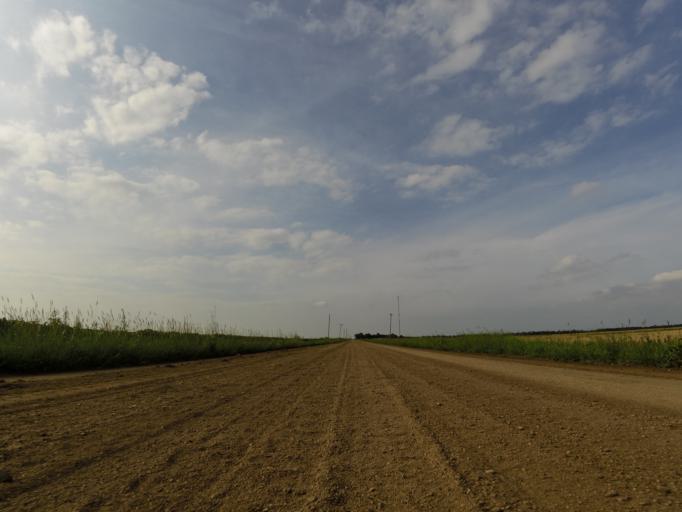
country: US
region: Kansas
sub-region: Reno County
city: South Hutchinson
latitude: 37.9659
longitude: -98.0688
